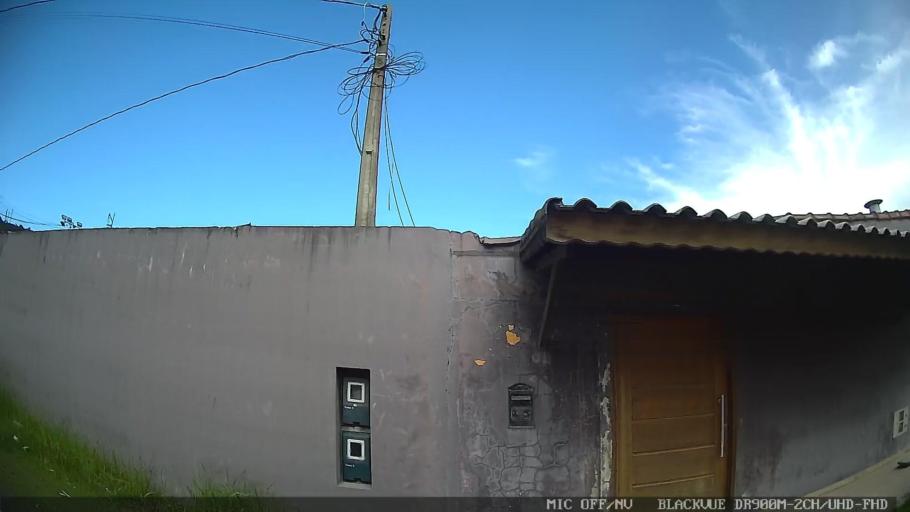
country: BR
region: Sao Paulo
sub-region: Iguape
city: Iguape
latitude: -24.7011
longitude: -47.5569
